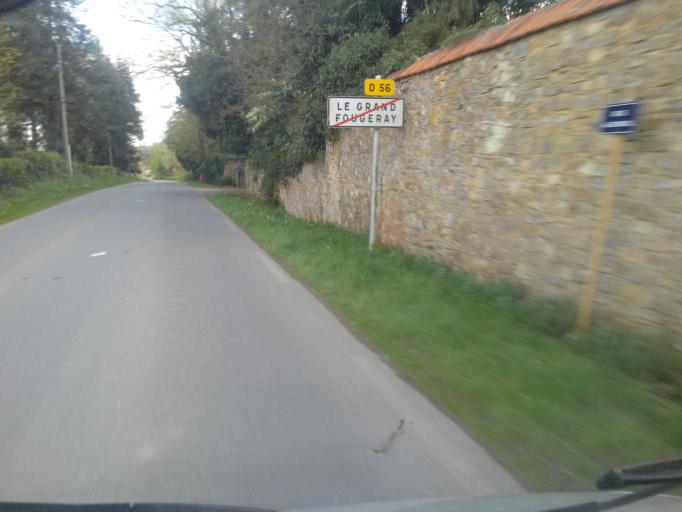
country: FR
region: Brittany
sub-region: Departement d'Ille-et-Vilaine
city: Grand-Fougeray
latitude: 47.7202
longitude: -1.7290
